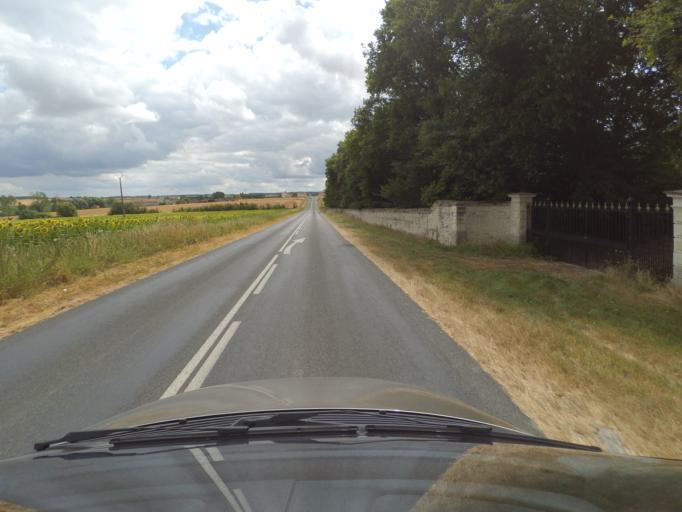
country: FR
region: Poitou-Charentes
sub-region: Departement de la Vienne
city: Saint-Gervais-les-Trois-Clochers
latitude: 46.9572
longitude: 0.3964
